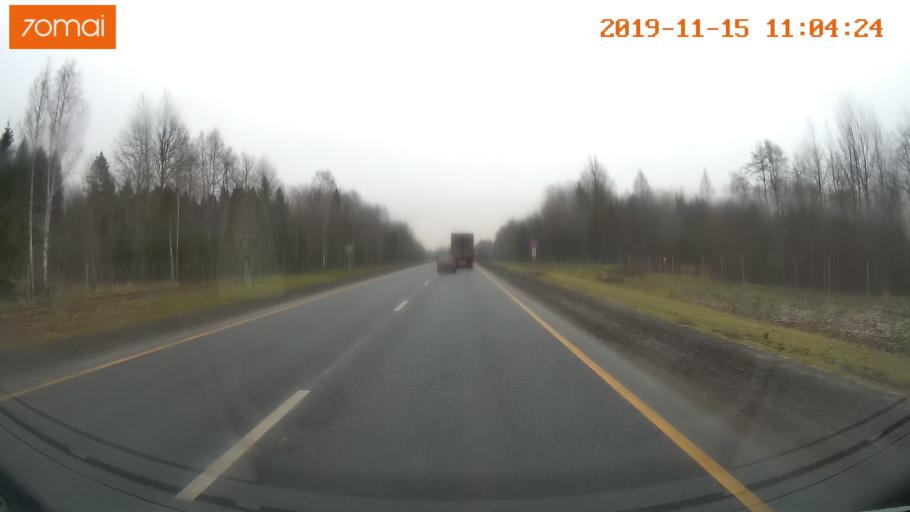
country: RU
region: Vologda
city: Chebsara
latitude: 59.1203
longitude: 38.9831
